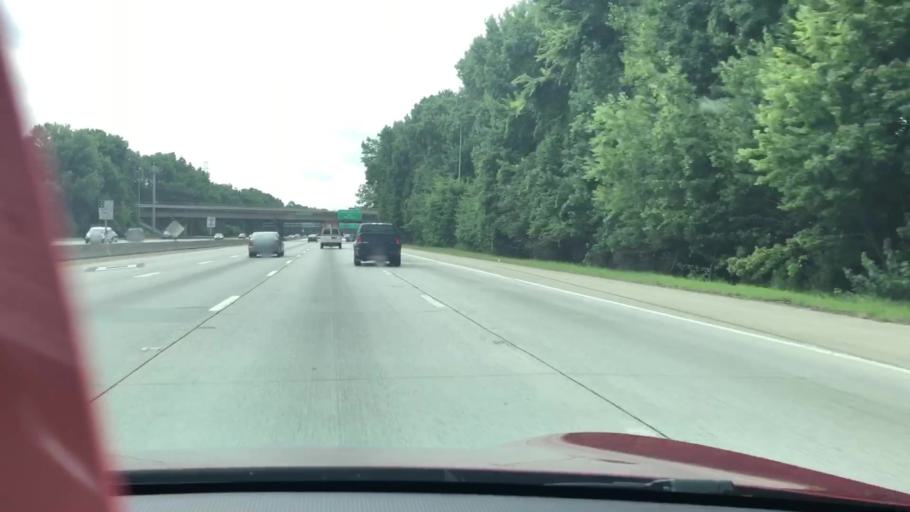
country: US
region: Virginia
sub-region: City of Chesapeake
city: Chesapeake
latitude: 36.8154
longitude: -76.1949
